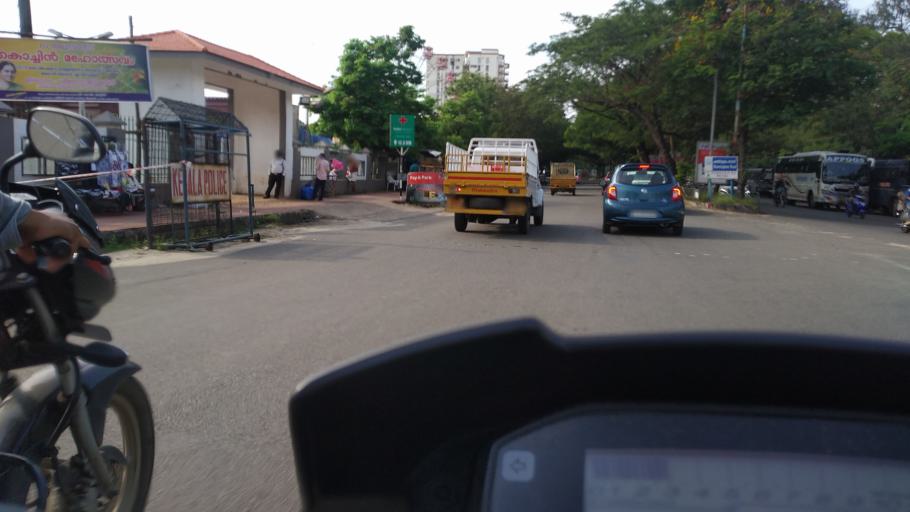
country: IN
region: Kerala
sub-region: Ernakulam
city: Cochin
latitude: 9.9809
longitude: 76.2754
